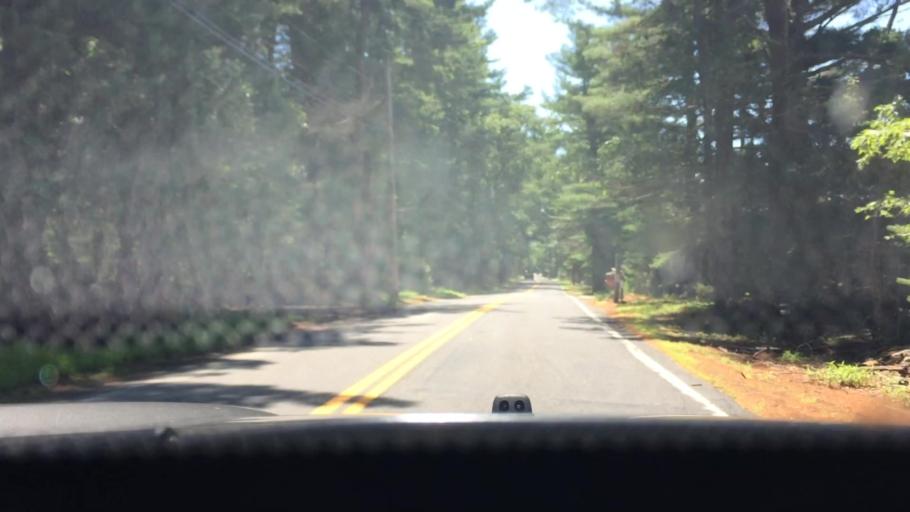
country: US
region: Rhode Island
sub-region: Providence County
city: Harrisville
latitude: 41.9906
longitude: -71.6831
